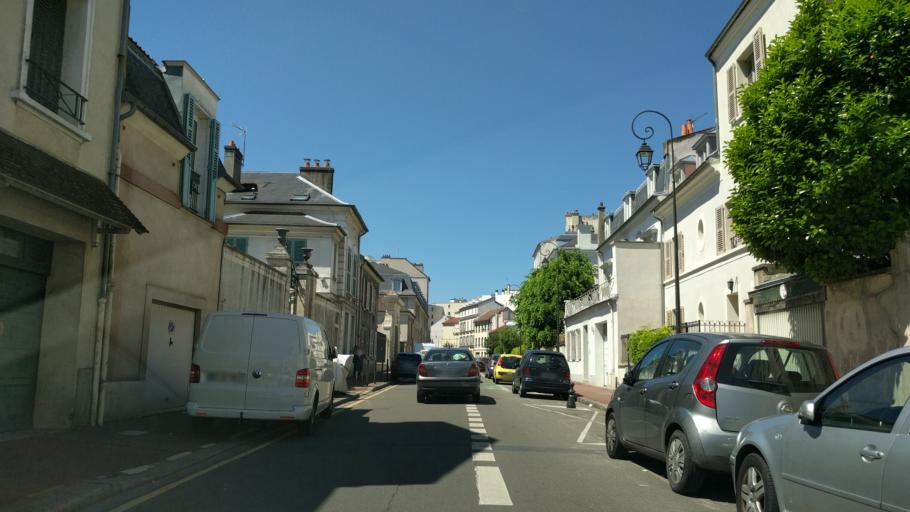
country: FR
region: Ile-de-France
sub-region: Departement des Yvelines
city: Le Pecq
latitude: 48.8936
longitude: 2.0955
